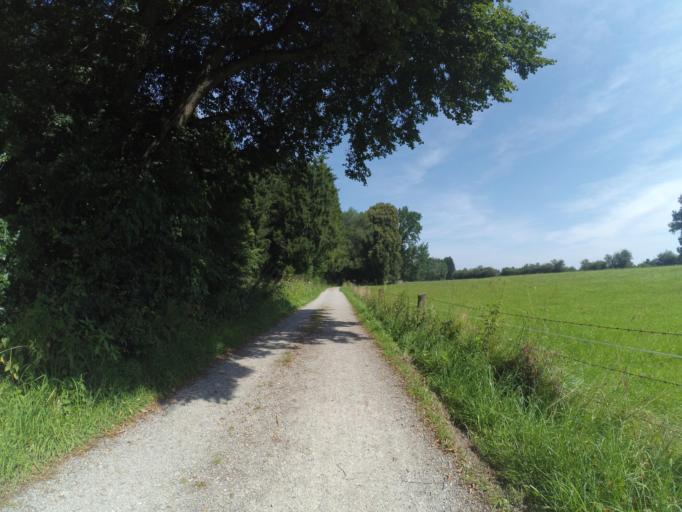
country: DE
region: Bavaria
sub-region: Swabia
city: Bad Worishofen
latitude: 47.9819
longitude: 10.5725
